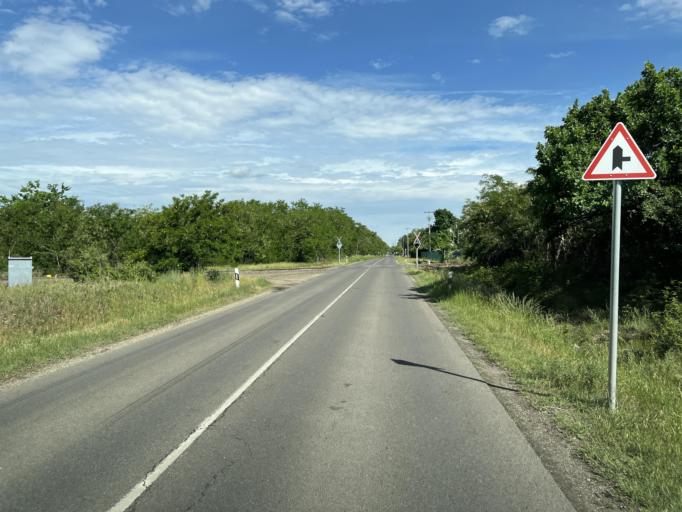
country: HU
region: Pest
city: Isaszeg
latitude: 47.5548
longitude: 19.3823
